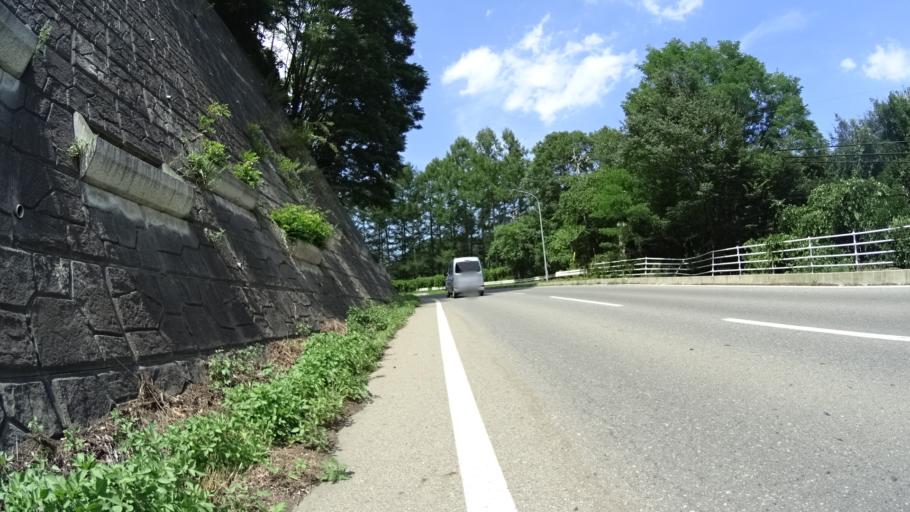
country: JP
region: Nagano
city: Saku
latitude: 36.0772
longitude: 138.4915
